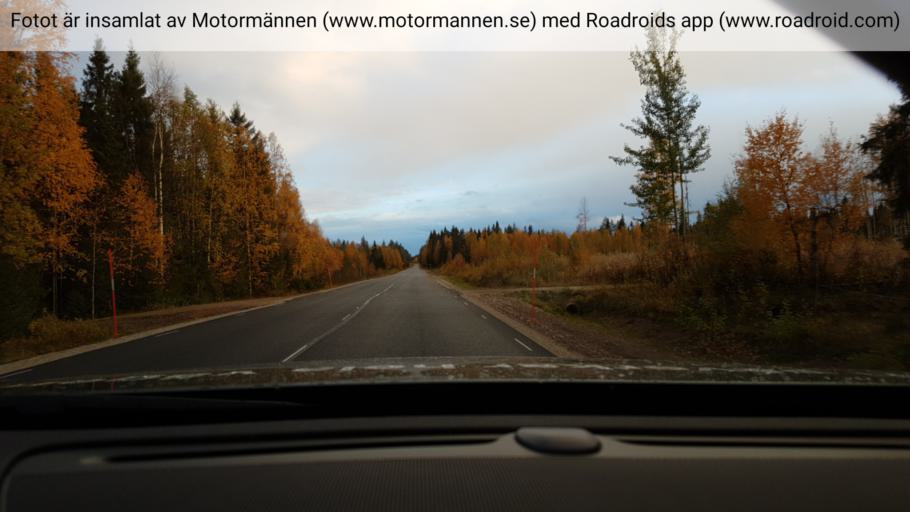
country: SE
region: Norrbotten
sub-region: Overkalix Kommun
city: OEverkalix
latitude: 66.4165
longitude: 22.8042
